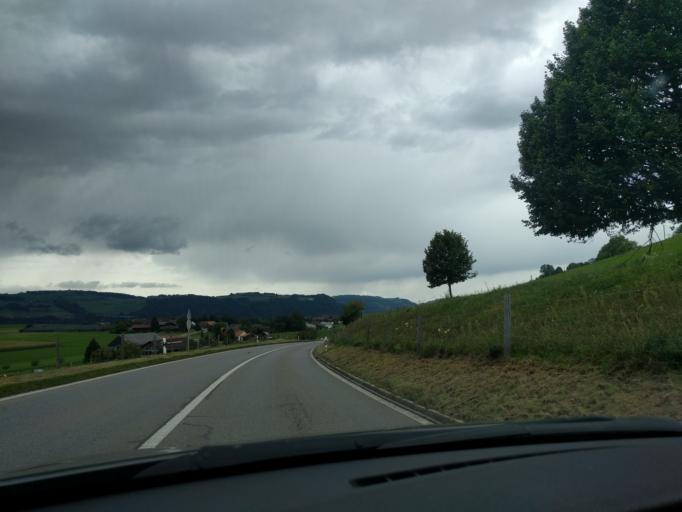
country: CH
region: Bern
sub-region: Bern-Mittelland District
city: Taegertschi
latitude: 46.8764
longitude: 7.5965
